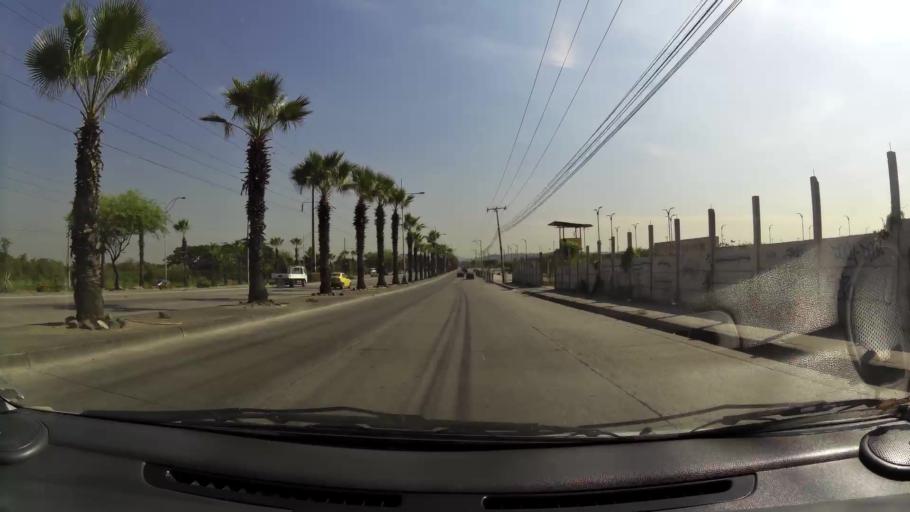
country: EC
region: Guayas
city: Eloy Alfaro
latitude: -2.1060
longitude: -79.9090
